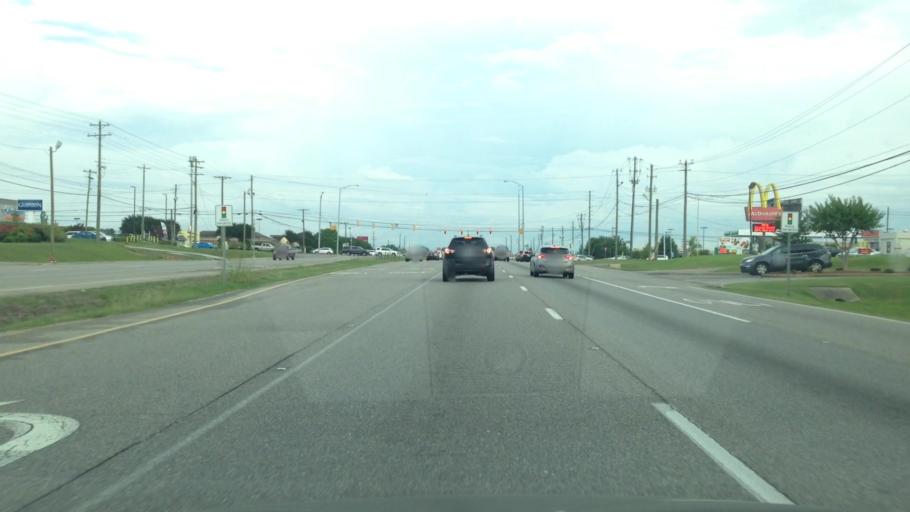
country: US
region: Alabama
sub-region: Montgomery County
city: Pike Road
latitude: 32.3405
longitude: -86.1795
